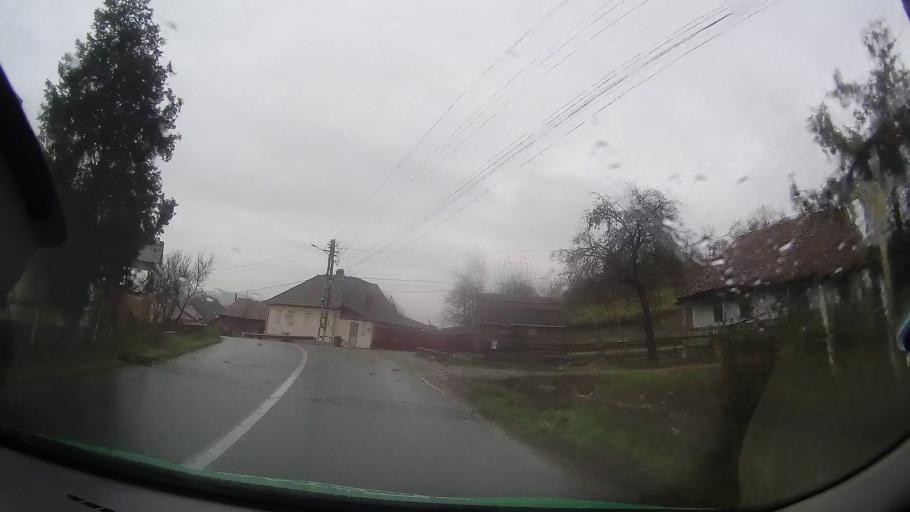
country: RO
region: Bistrita-Nasaud
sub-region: Comuna Mariselu
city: Mariselu
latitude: 47.0139
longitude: 24.5100
